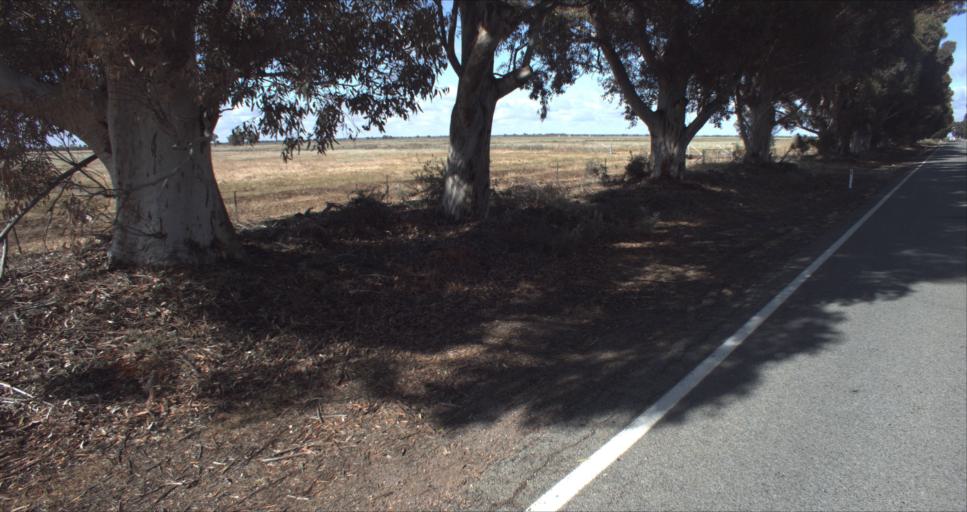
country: AU
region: New South Wales
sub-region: Leeton
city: Leeton
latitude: -34.5463
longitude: 146.3261
